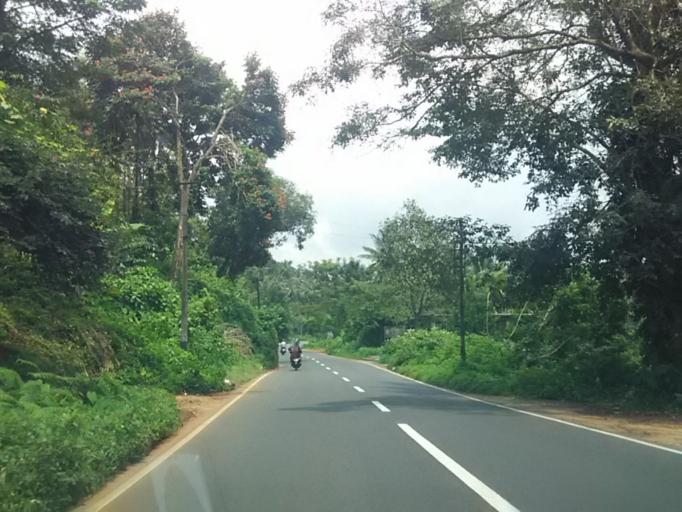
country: IN
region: Kerala
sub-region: Wayanad
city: Kalpetta
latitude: 11.5347
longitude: 76.0332
